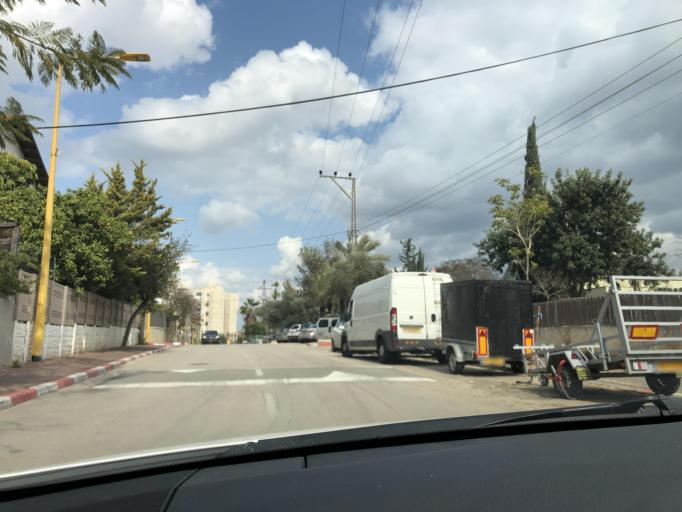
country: IL
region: Central District
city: Ganne Tiqwa
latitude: 32.0576
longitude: 34.8778
